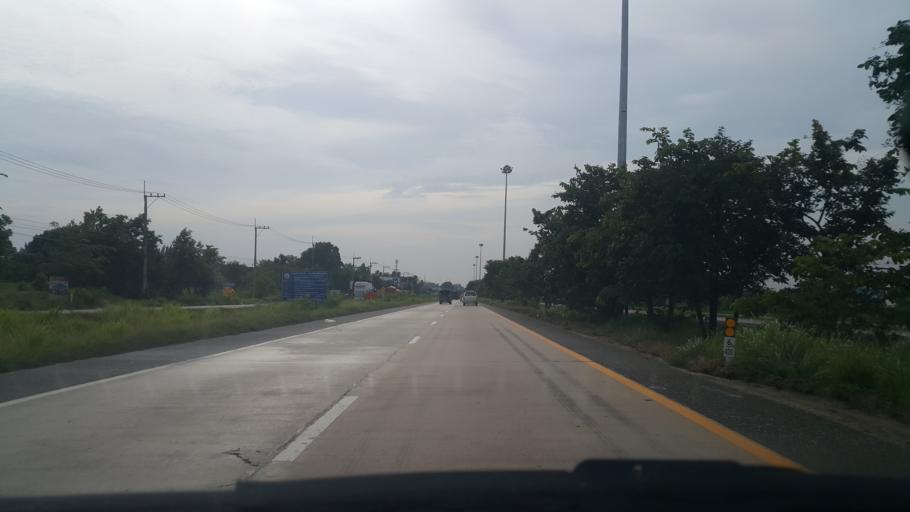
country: TH
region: Chon Buri
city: Bang Lamung
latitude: 12.9677
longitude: 100.9770
